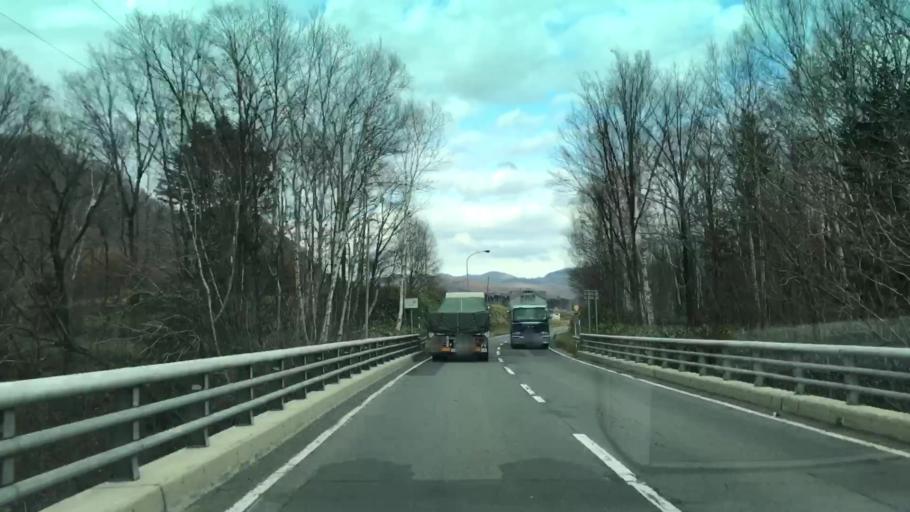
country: JP
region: Hokkaido
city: Shimo-furano
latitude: 42.8575
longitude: 142.4163
